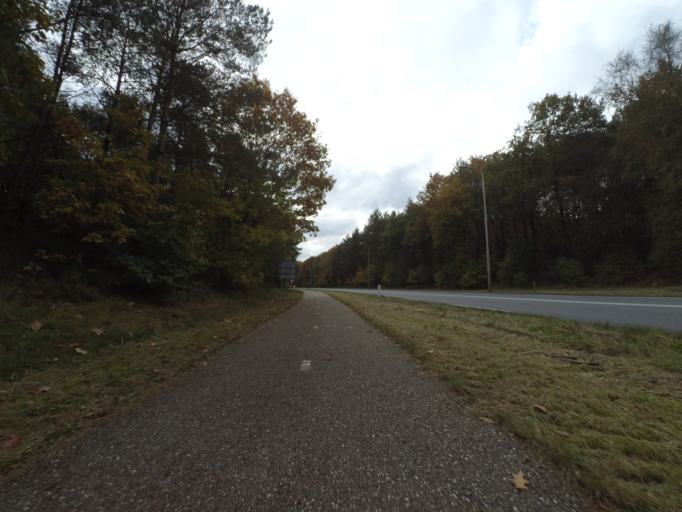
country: NL
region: Gelderland
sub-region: Gemeente Ermelo
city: Ermelo
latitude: 52.3017
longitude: 5.6792
